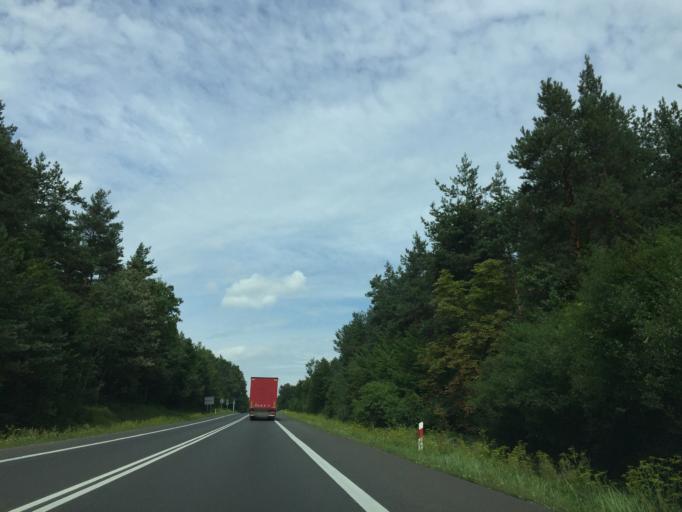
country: PL
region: Lesser Poland Voivodeship
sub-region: Powiat olkuski
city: Osiek
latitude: 50.2611
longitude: 19.6256
